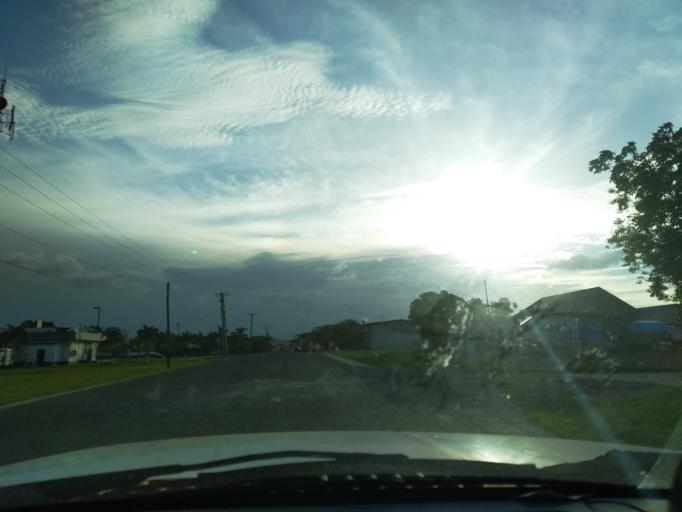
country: BZ
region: Cayo
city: San Ignacio
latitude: 17.2567
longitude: -89.0008
